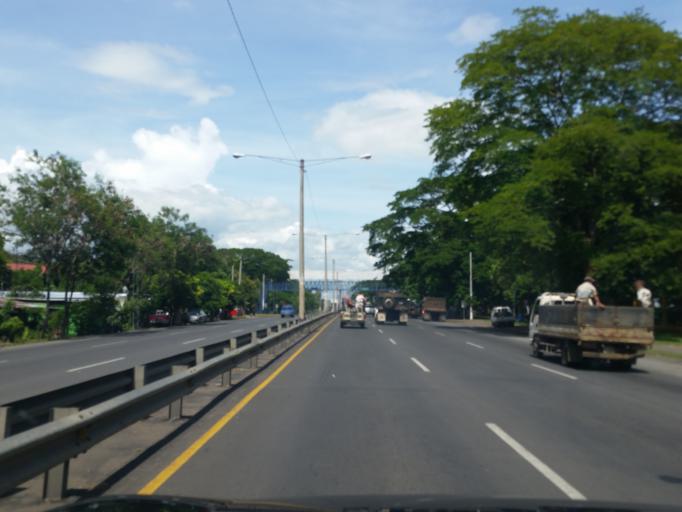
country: NI
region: Managua
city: Tipitapa
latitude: 12.1464
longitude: -86.1633
